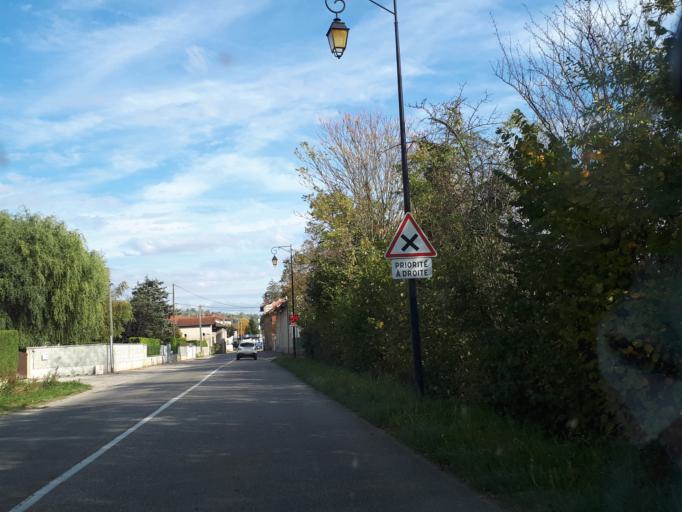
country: FR
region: Rhone-Alpes
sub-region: Departement de l'Isere
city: Saint-Savin
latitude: 45.6268
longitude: 5.3017
